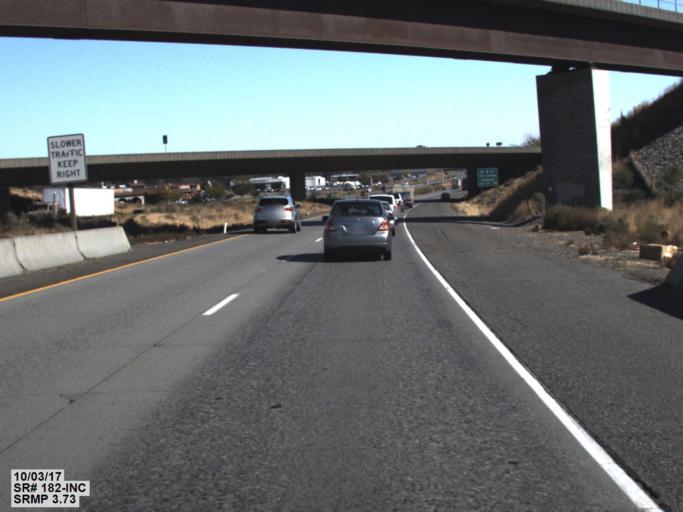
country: US
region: Washington
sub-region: Benton County
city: Richland
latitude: 46.2586
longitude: -119.2884
